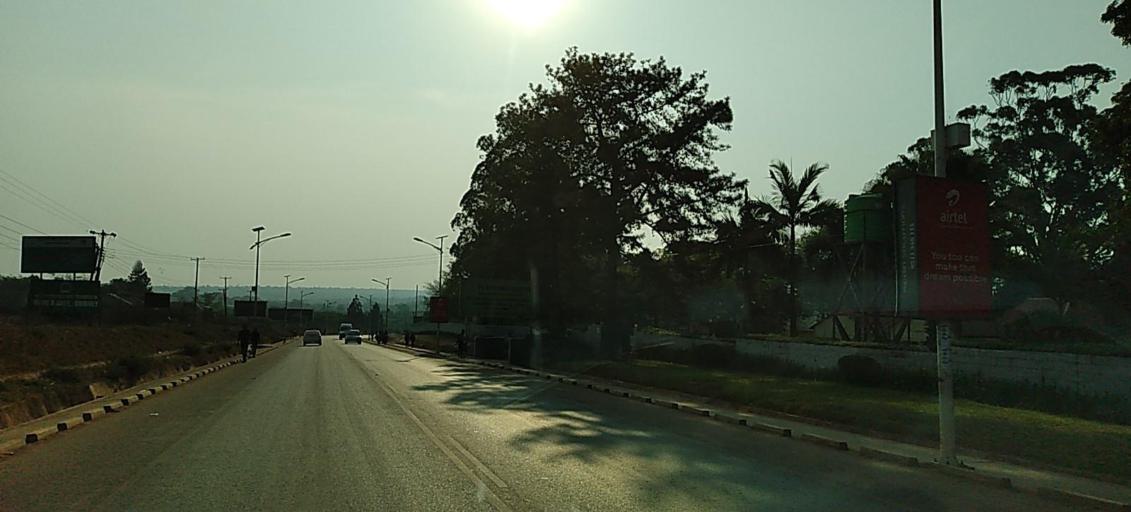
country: ZM
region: North-Western
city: Solwezi
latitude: -12.1887
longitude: 26.4280
